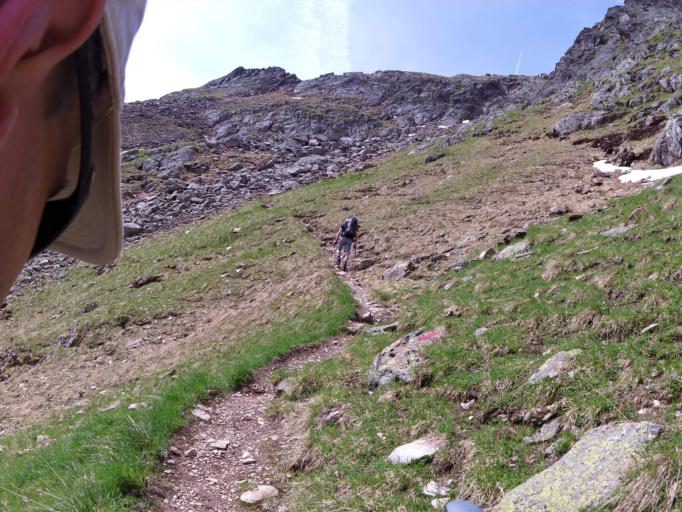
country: AT
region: Tyrol
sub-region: Politischer Bezirk Innsbruck Land
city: Gschnitz
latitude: 47.0263
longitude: 11.2895
